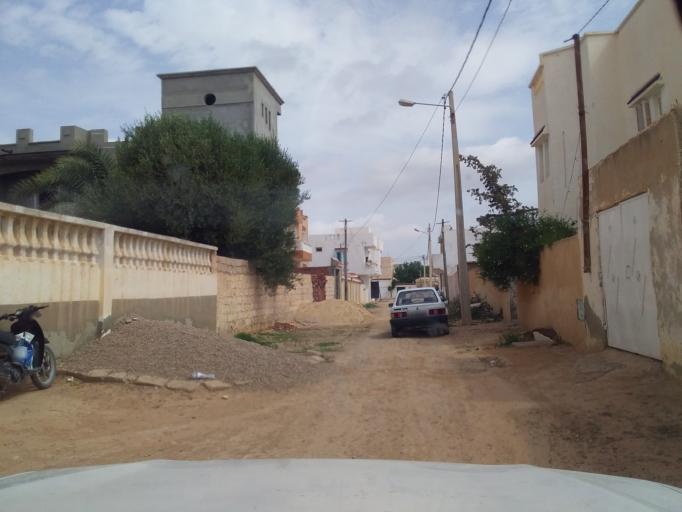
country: TN
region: Qabis
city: Gabes
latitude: 33.6169
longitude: 10.2941
